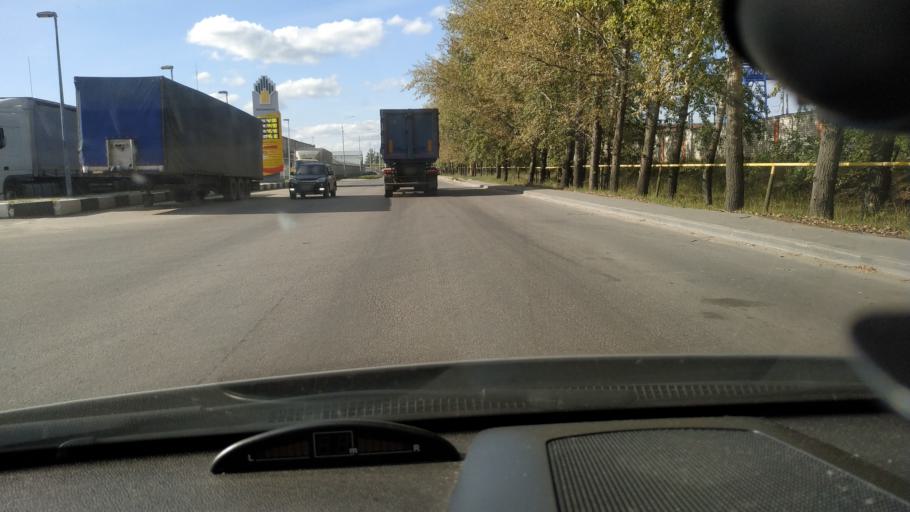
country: RU
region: Rjazan
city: Ryazan'
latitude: 54.6534
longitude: 39.6414
